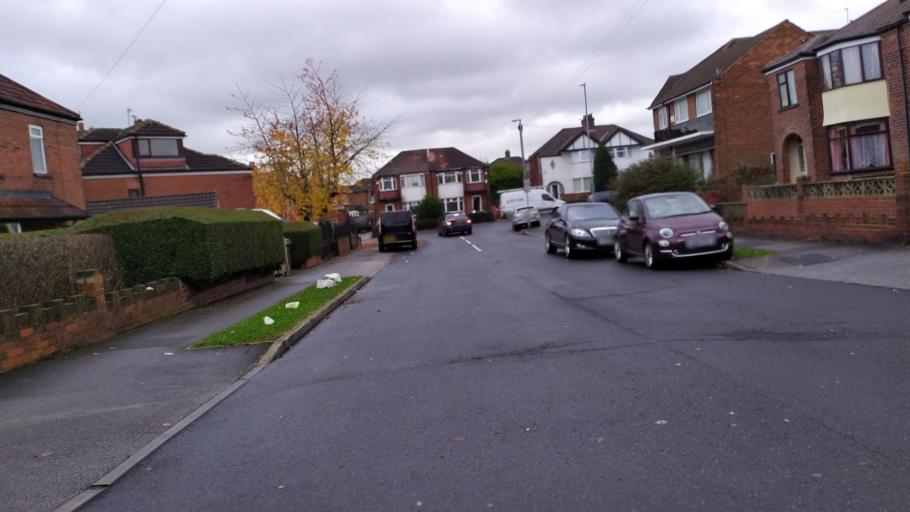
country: GB
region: England
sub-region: City and Borough of Leeds
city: Leeds
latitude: 53.8151
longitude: -1.5924
